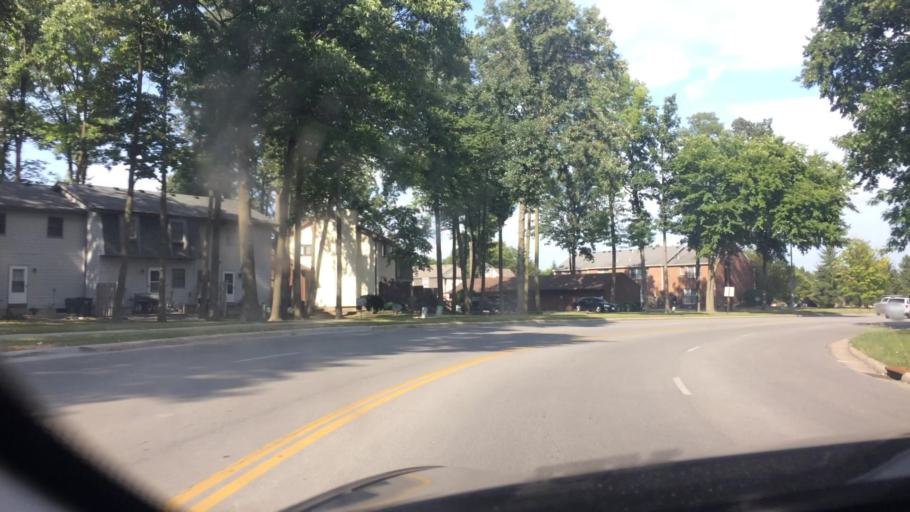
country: US
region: Ohio
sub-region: Lucas County
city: Maumee
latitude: 41.5854
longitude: -83.6599
